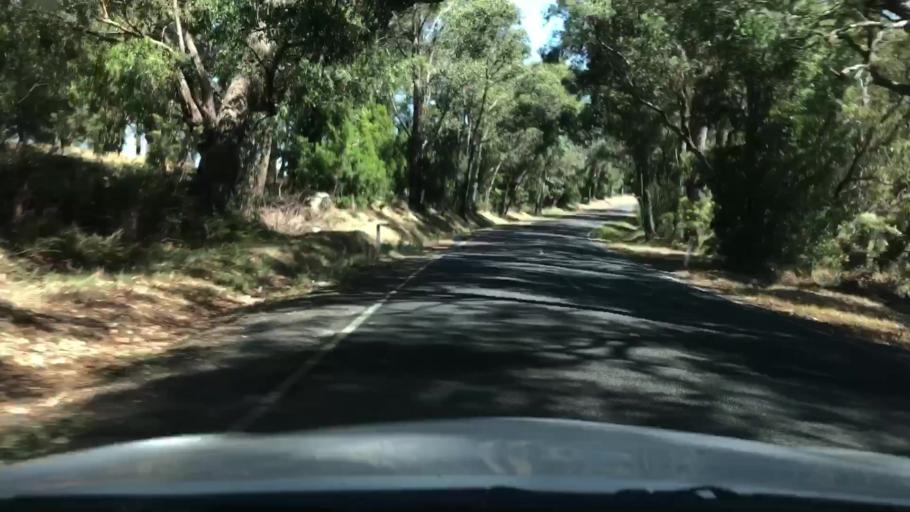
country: AU
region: Victoria
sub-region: Yarra Ranges
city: Macclesfield
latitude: -37.8682
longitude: 145.4796
